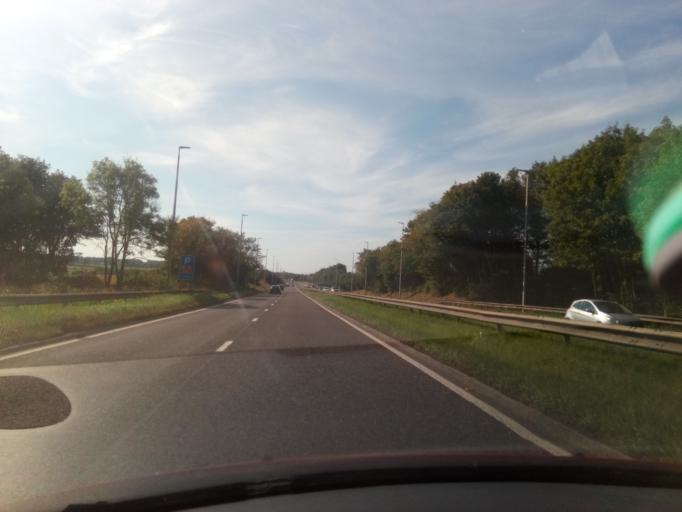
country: GB
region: England
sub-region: County Durham
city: Shotton
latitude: 54.7719
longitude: -1.3577
